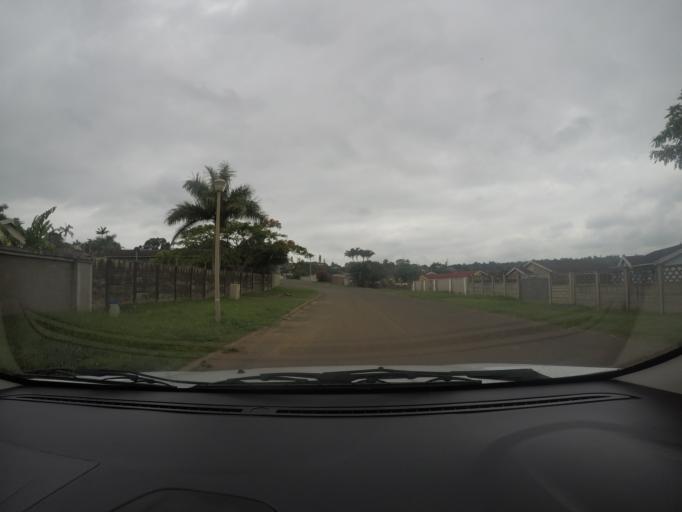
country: ZA
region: KwaZulu-Natal
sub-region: uThungulu District Municipality
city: Empangeni
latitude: -28.7625
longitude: 31.8822
